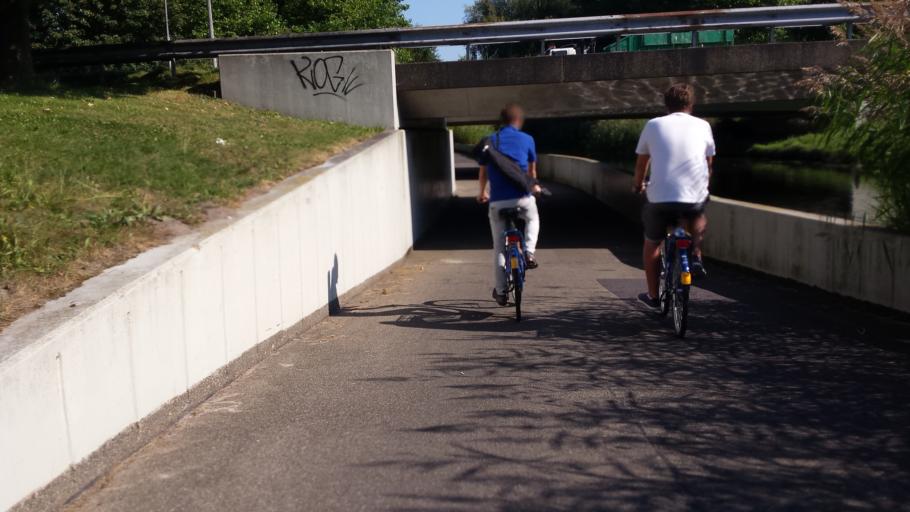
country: NL
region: Flevoland
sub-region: Gemeente Almere
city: Almere Stad
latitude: 52.3447
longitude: 5.2201
